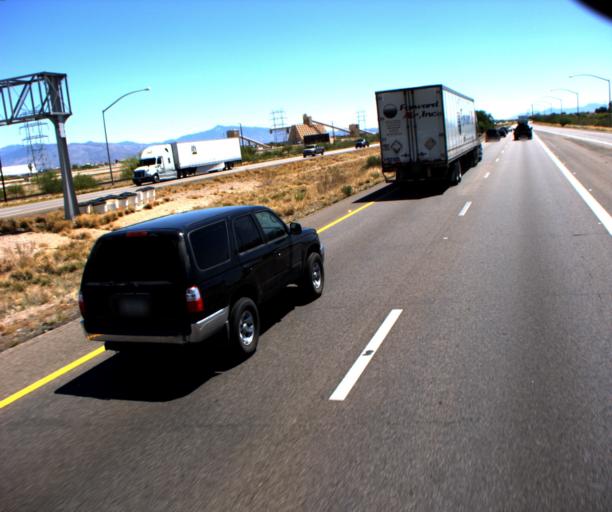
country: US
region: Arizona
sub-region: Pima County
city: Tucson
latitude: 32.1549
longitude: -110.9051
